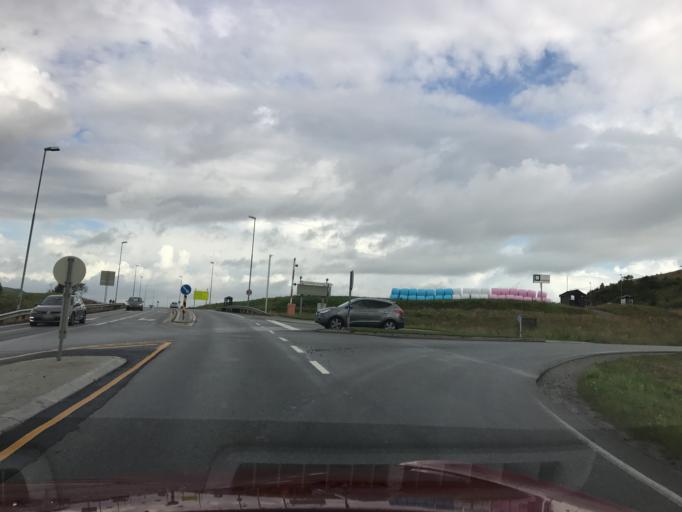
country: NO
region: Rogaland
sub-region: Rennesoy
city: Vikevag
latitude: 59.0641
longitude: 5.6767
